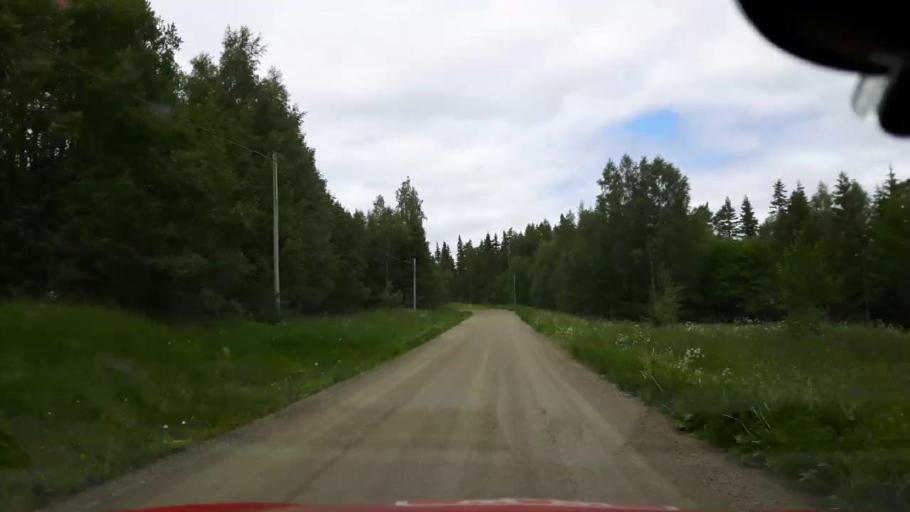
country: SE
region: Jaemtland
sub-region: OEstersunds Kommun
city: Brunflo
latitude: 62.9044
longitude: 15.1087
